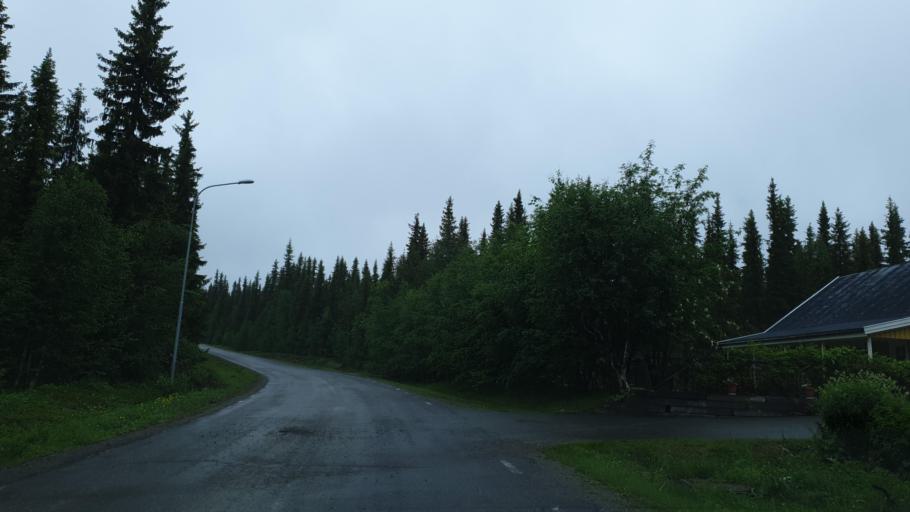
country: SE
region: Vaesterbotten
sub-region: Vilhelmina Kommun
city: Sjoberg
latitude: 65.2395
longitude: 15.9924
